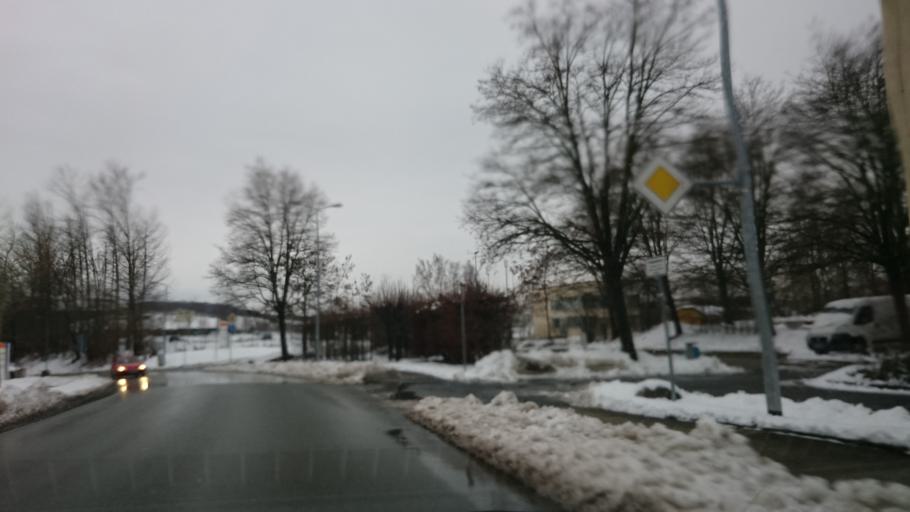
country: DE
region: Saxony
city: Sankt Egidien
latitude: 50.7908
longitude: 12.6256
